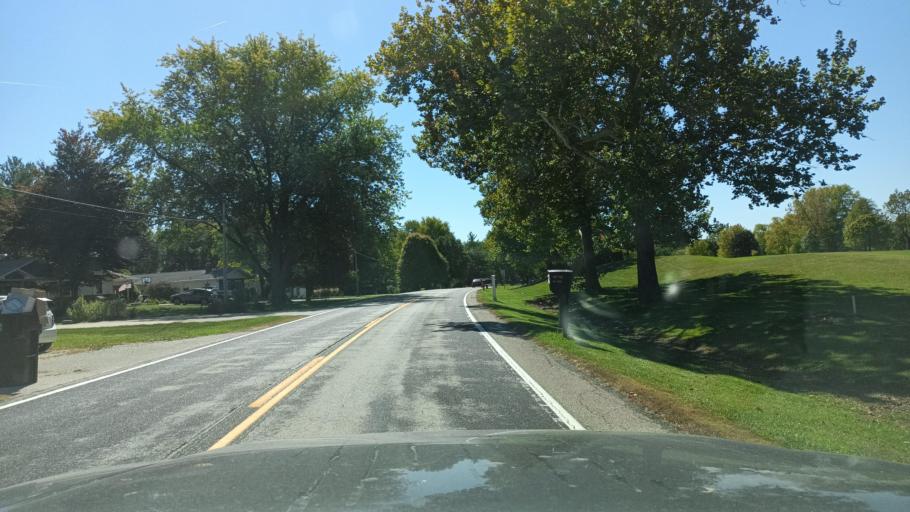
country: US
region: Illinois
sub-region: Champaign County
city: Lake of the Woods
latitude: 40.2031
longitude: -88.3717
